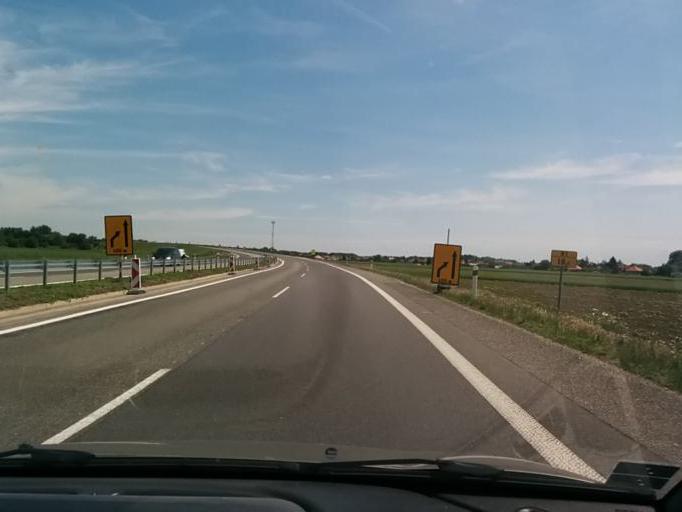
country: SK
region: Trnavsky
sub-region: Okres Galanta
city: Galanta
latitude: 48.2560
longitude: 17.7686
